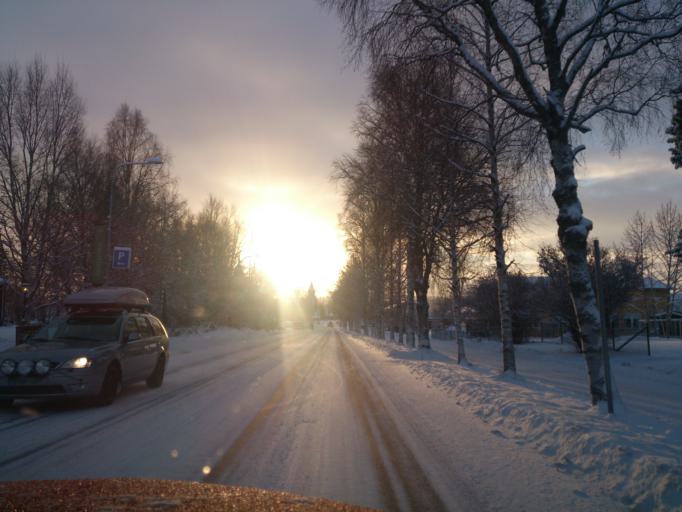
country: SE
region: Jaemtland
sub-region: Harjedalens Kommun
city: Sveg
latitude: 62.4477
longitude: 13.8628
